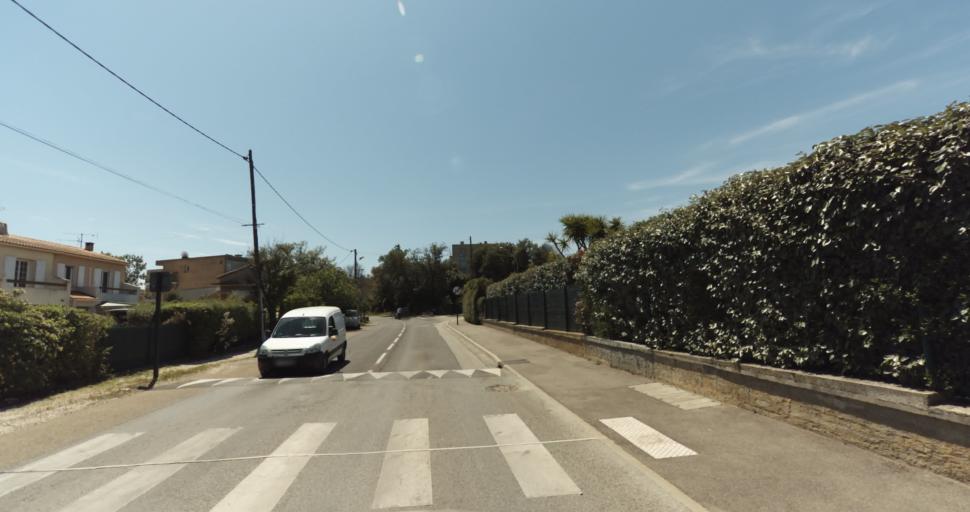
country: FR
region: Provence-Alpes-Cote d'Azur
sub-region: Departement du Var
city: Hyeres
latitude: 43.1265
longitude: 6.1521
